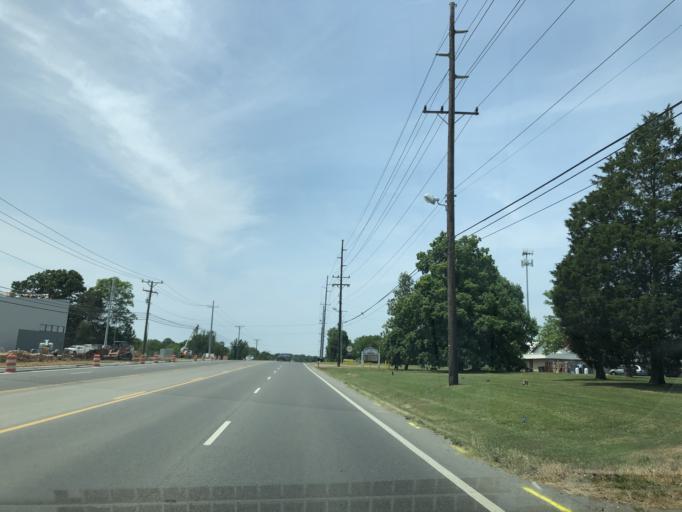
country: US
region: Tennessee
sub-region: Rutherford County
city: La Vergne
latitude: 36.0466
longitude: -86.6107
